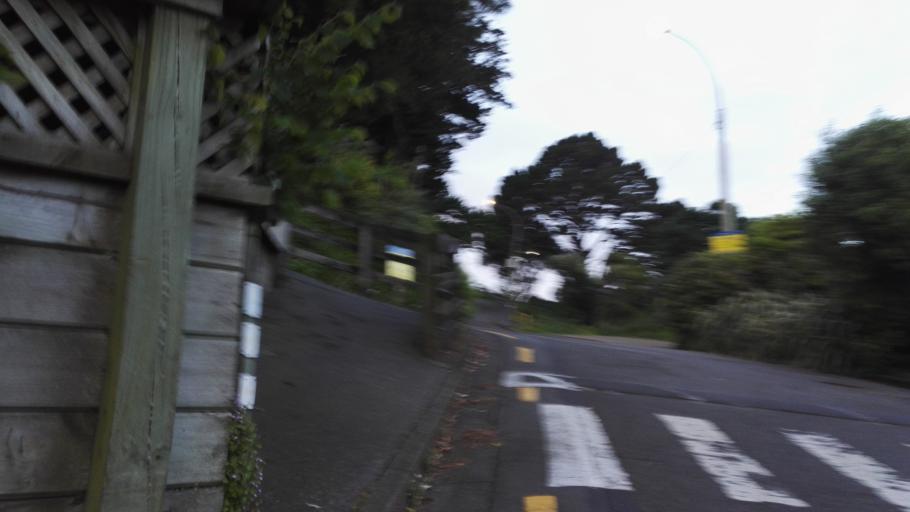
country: NZ
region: Wellington
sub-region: Wellington City
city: Wellington
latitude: -41.2936
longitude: 174.7694
